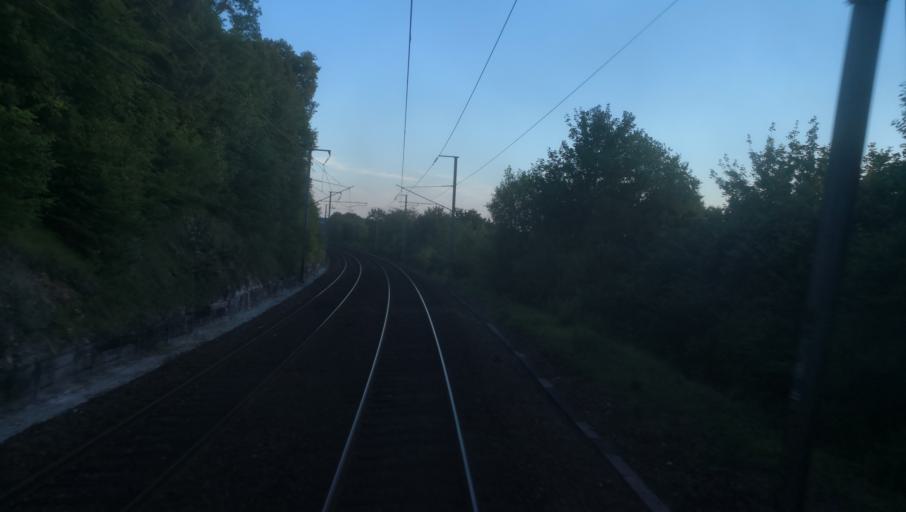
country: FR
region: Haute-Normandie
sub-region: Departement de l'Eure
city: Arnieres-sur-Iton
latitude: 49.0117
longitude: 1.1190
